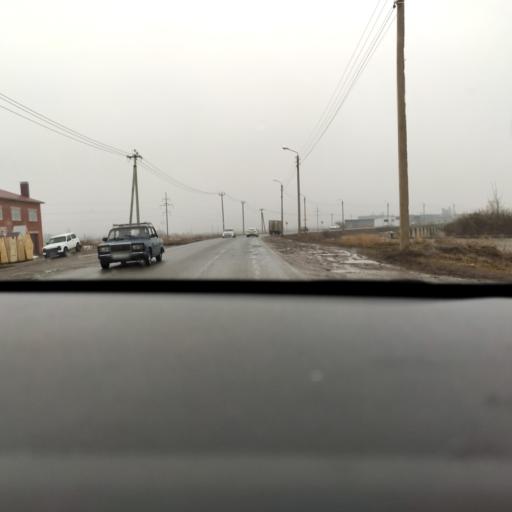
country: RU
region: Tatarstan
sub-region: Chistopol'skiy Rayon
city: Chistopol'
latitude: 55.3459
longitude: 50.6588
